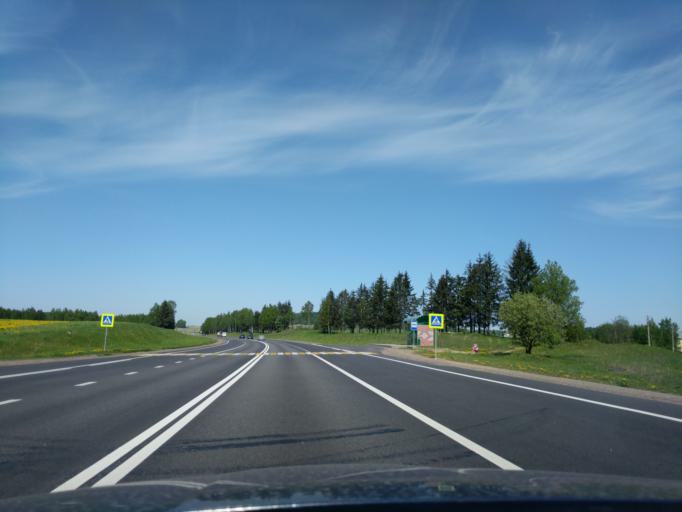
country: BY
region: Minsk
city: Bal'shavik
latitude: 54.0859
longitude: 27.5511
